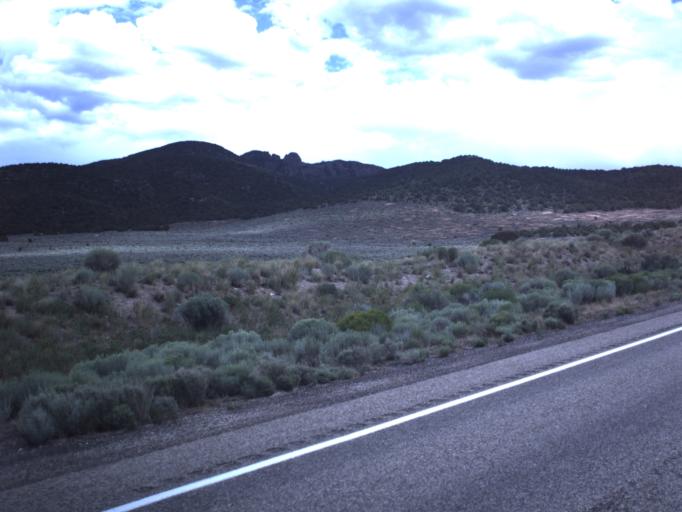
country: US
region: Utah
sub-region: Beaver County
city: Beaver
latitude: 38.0511
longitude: -112.5770
